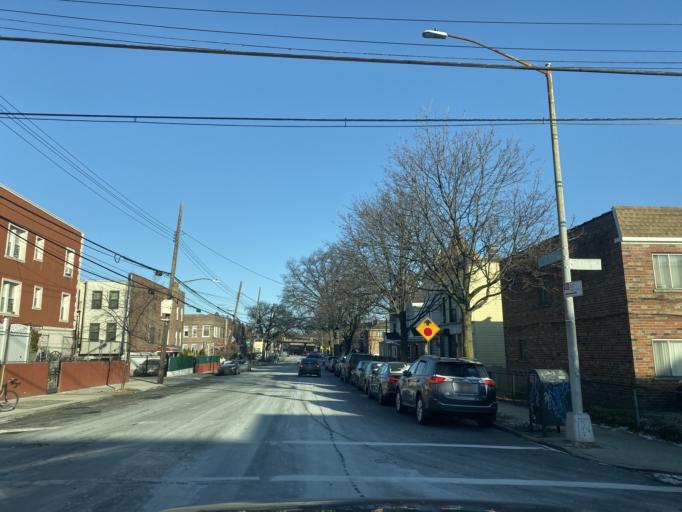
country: US
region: New York
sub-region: Bronx
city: The Bronx
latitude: 40.8331
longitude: -73.8481
